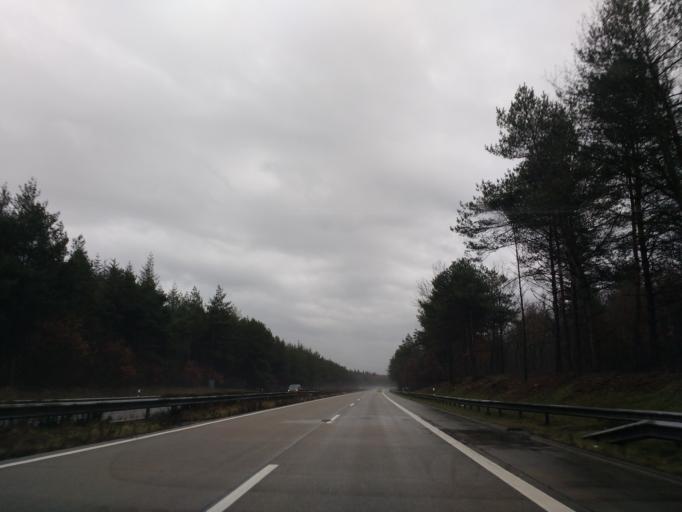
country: DE
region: Lower Saxony
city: Midlum
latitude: 53.7061
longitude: 8.6635
